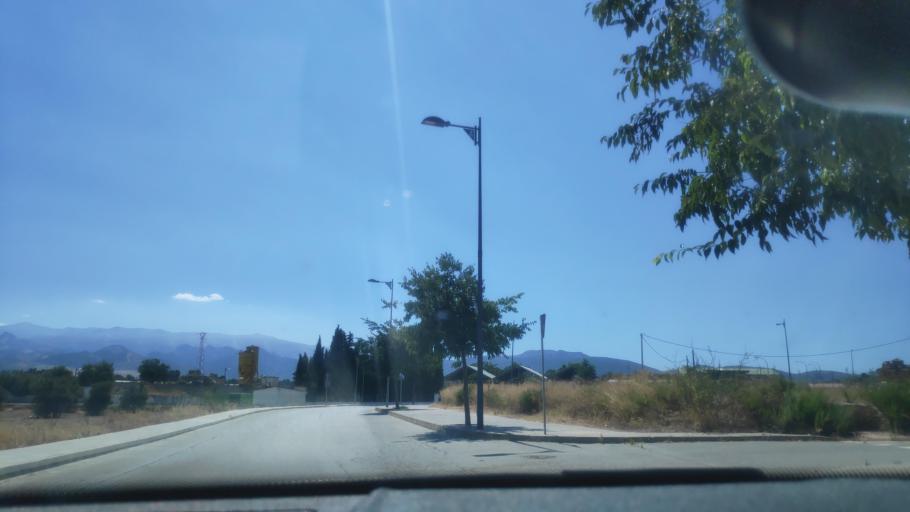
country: ES
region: Andalusia
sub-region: Provincia de Granada
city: Alhendin
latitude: 37.1030
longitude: -3.6521
